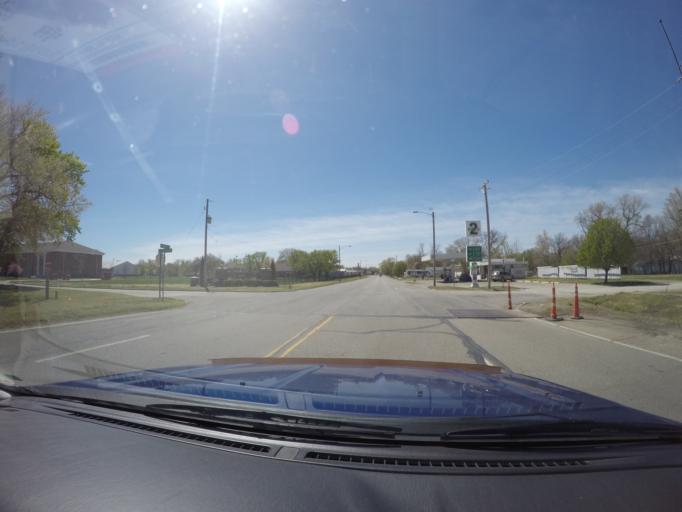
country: US
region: Kansas
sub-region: Saline County
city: Salina
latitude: 38.8636
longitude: -97.6124
